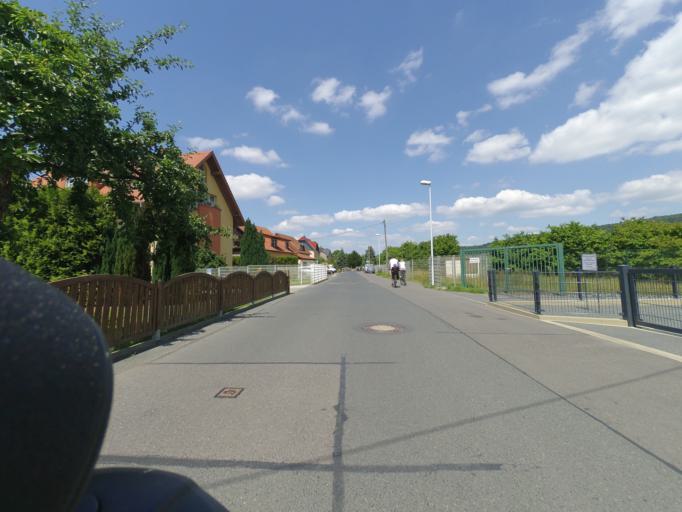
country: DE
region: Saxony
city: Heidenau
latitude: 50.9964
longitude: 13.8804
